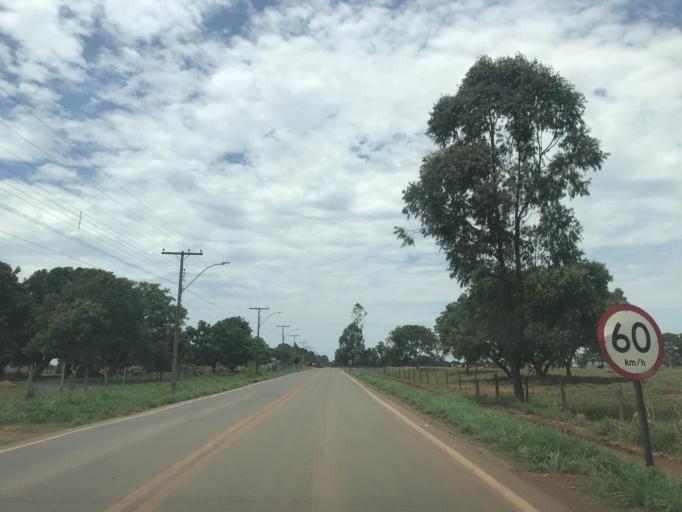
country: BR
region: Goias
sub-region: Luziania
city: Luziania
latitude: -16.3148
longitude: -48.0157
